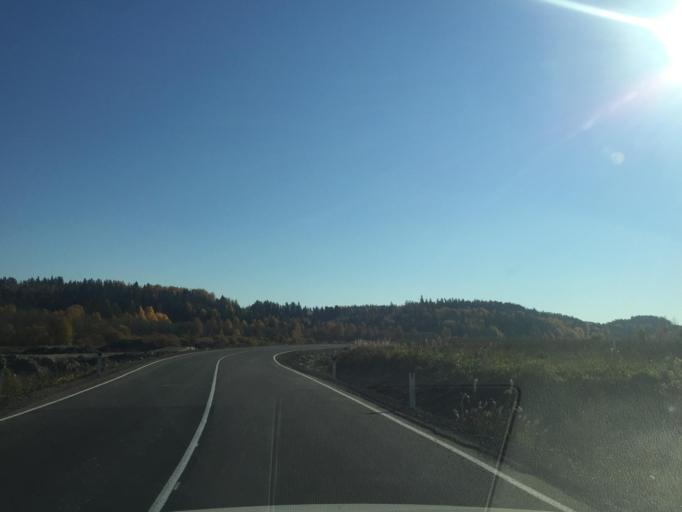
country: RU
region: Leningrad
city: Kuznechnoye
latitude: 61.3367
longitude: 29.8633
